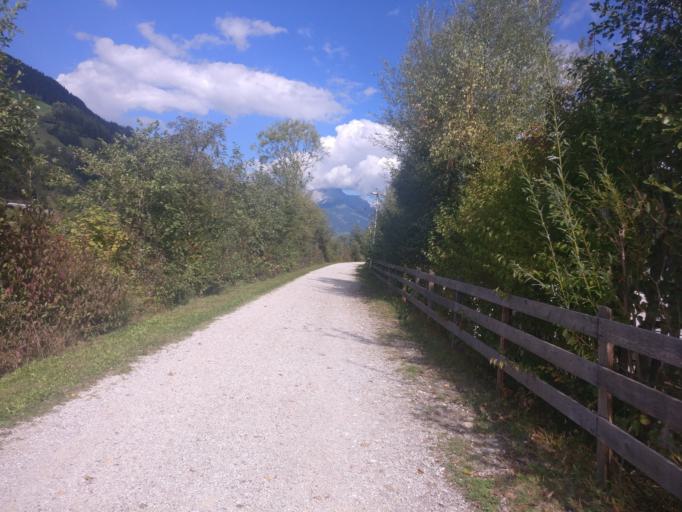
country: AT
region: Salzburg
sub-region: Politischer Bezirk Sankt Johann im Pongau
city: Sankt Johann im Pongau
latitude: 47.3655
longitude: 13.2084
